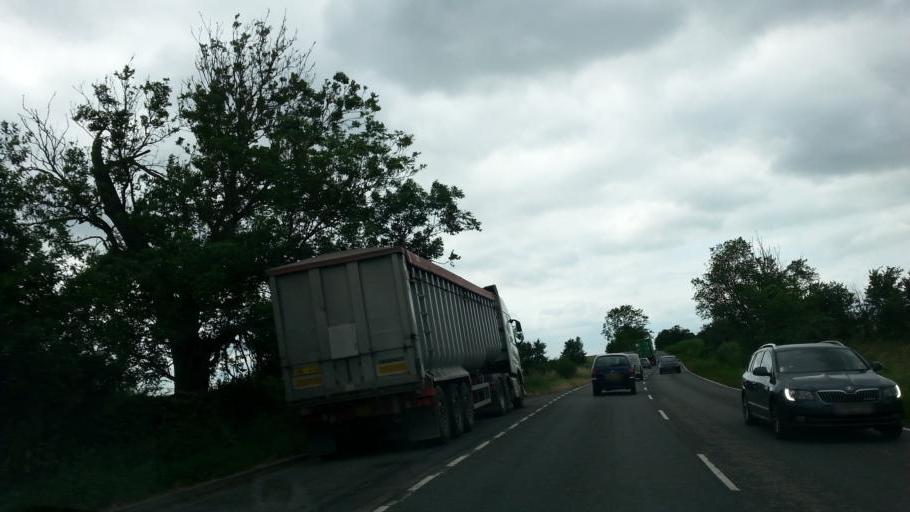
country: GB
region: England
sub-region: Cambridgeshire
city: Godmanchester
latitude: 52.3037
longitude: -0.1592
